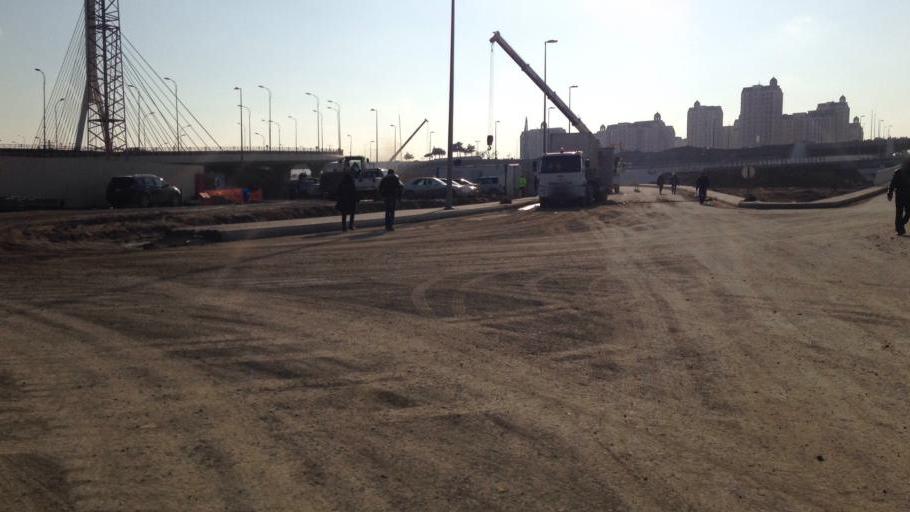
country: AZ
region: Baki
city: Sabuncu
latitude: 40.4269
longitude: 49.9211
